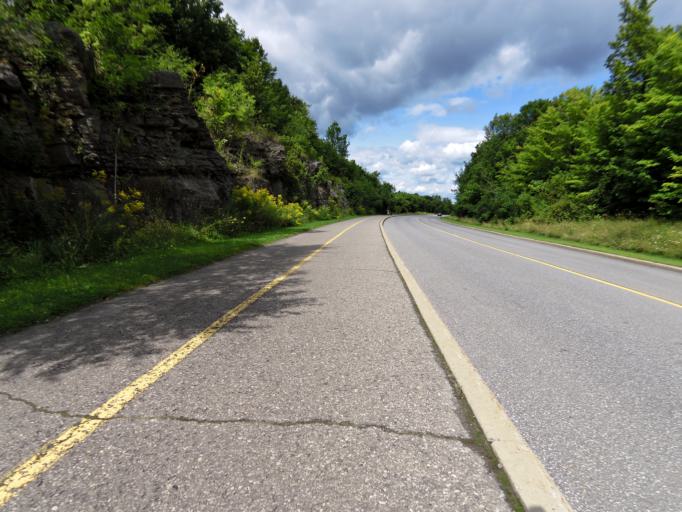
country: CA
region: Quebec
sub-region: Outaouais
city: Gatineau
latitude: 45.4477
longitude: -75.6449
